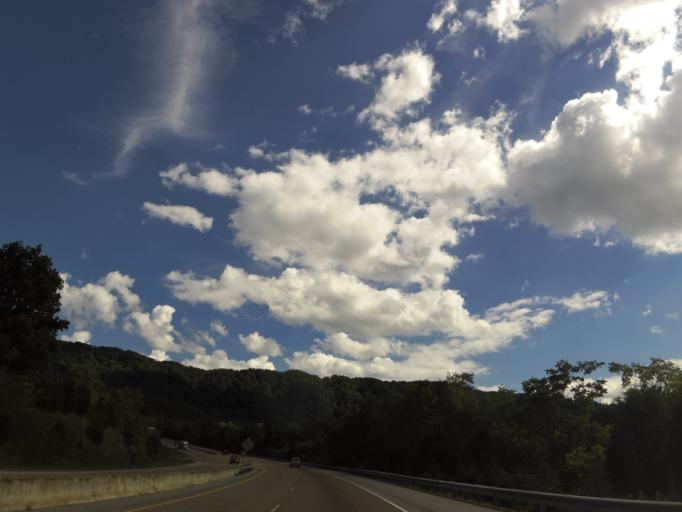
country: US
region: Tennessee
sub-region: Grainger County
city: Rutledge
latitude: 36.3524
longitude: -83.4351
